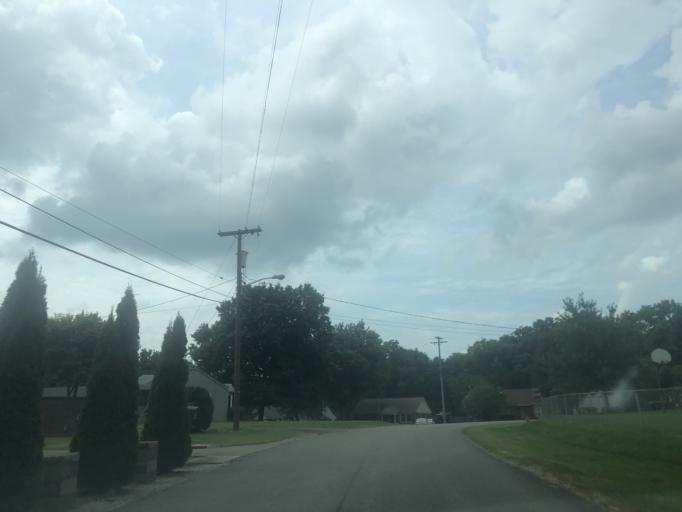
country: US
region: Tennessee
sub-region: Davidson County
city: Nashville
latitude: 36.1579
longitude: -86.6880
